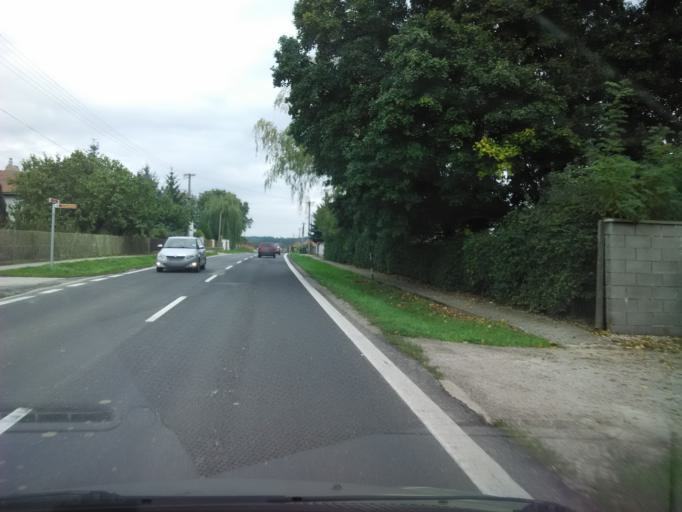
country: SK
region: Nitriansky
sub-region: Okres Nitra
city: Vrable
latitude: 48.2318
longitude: 18.3946
